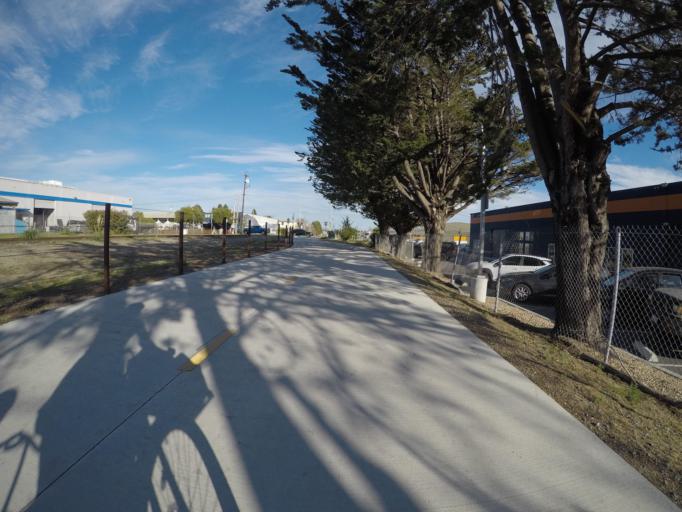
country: US
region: California
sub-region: Santa Cruz County
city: Santa Cruz
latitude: 36.9593
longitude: -122.0499
